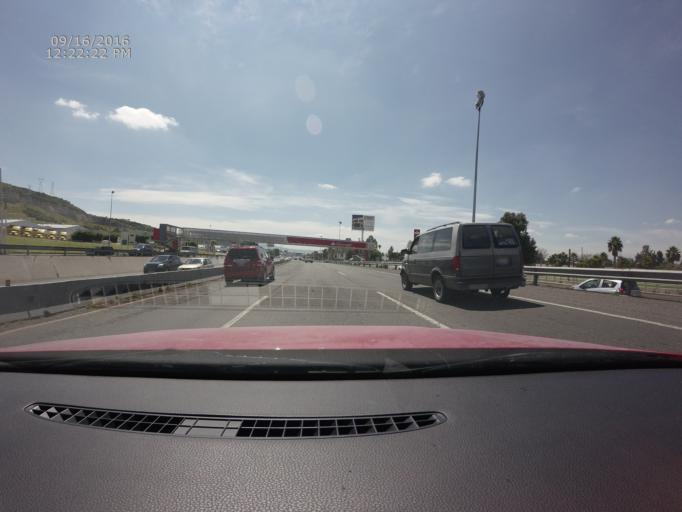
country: MX
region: Queretaro
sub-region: Queretaro
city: Sergio Villasenor
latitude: 20.6396
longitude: -100.4302
